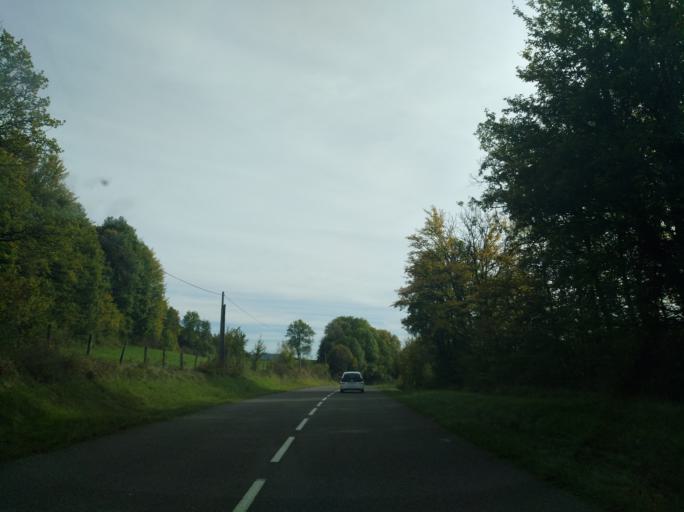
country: FR
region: Bourgogne
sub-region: Departement de Saone-et-Loire
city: Cuiseaux
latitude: 46.4553
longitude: 5.4147
